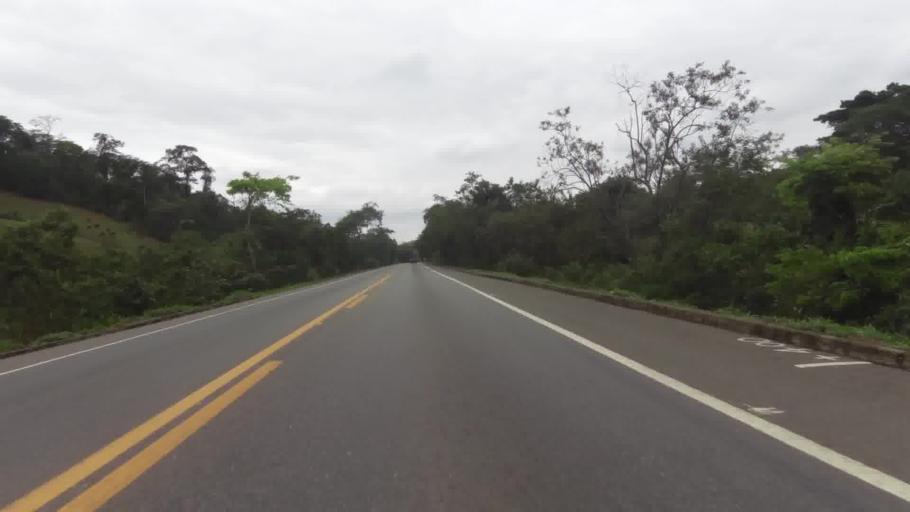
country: BR
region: Espirito Santo
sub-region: Iconha
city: Iconha
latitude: -20.7820
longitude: -40.7810
